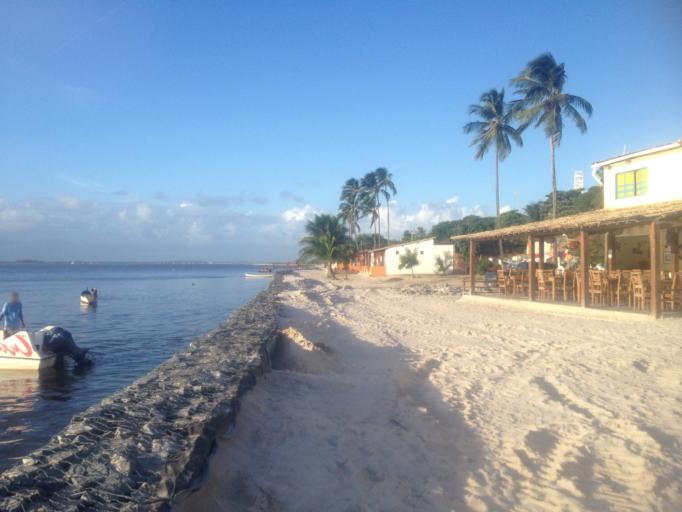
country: BR
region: Sergipe
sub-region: Indiaroba
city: Indiaroba
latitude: -11.4640
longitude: -37.3688
